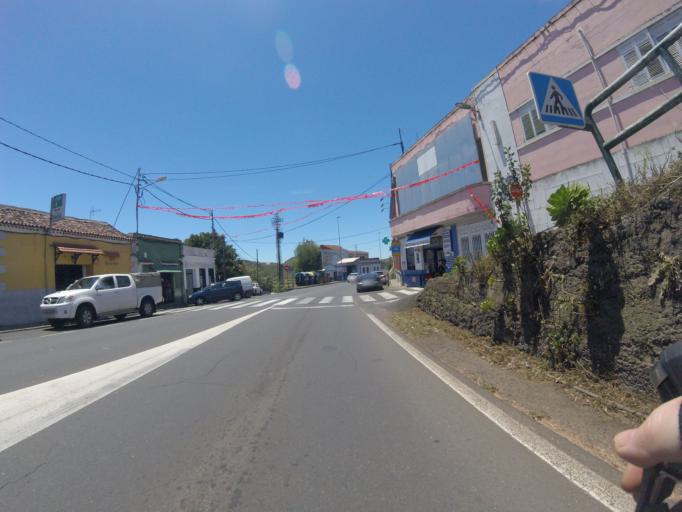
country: ES
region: Canary Islands
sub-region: Provincia de Santa Cruz de Tenerife
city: Tegueste
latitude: 28.5127
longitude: -16.3062
